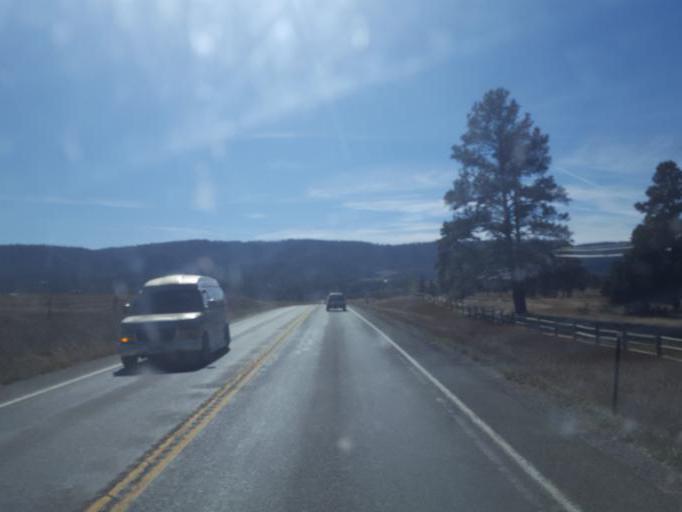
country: US
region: Colorado
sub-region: Archuleta County
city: Pagosa Springs
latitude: 37.2403
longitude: -107.1007
